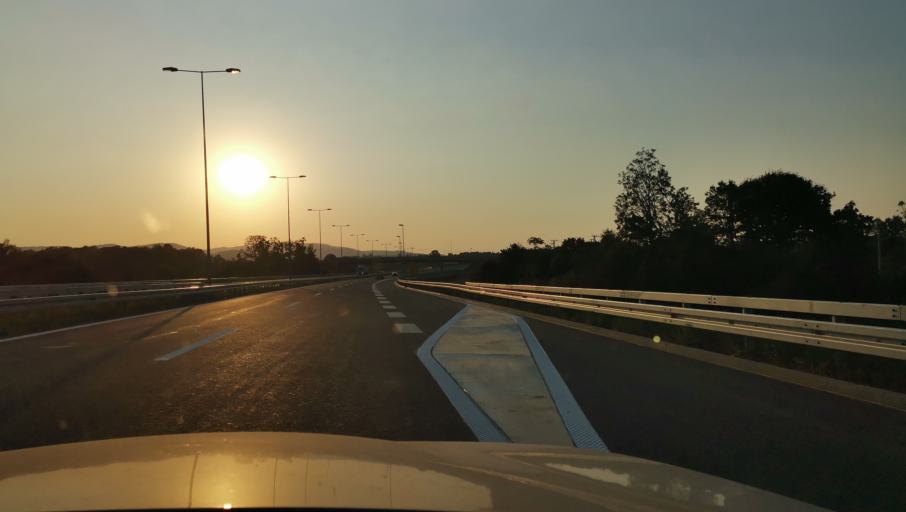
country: RS
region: Central Serbia
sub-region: Kolubarski Okrug
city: Lajkovac
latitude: 44.3561
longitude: 20.1336
